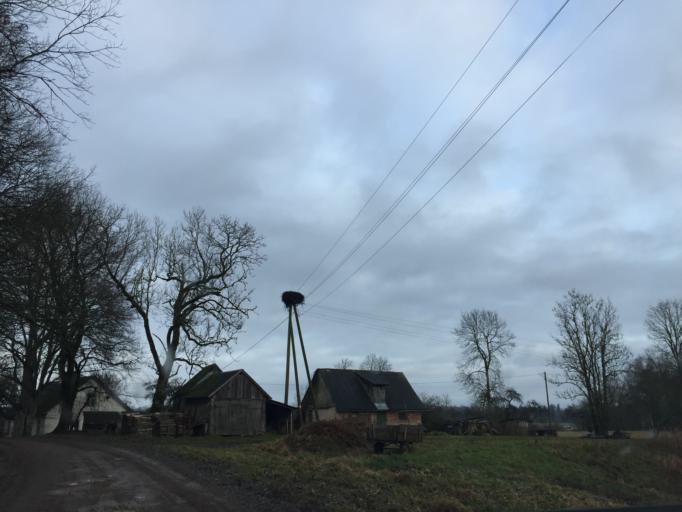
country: LV
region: Vainode
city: Vainode
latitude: 56.6148
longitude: 21.7951
